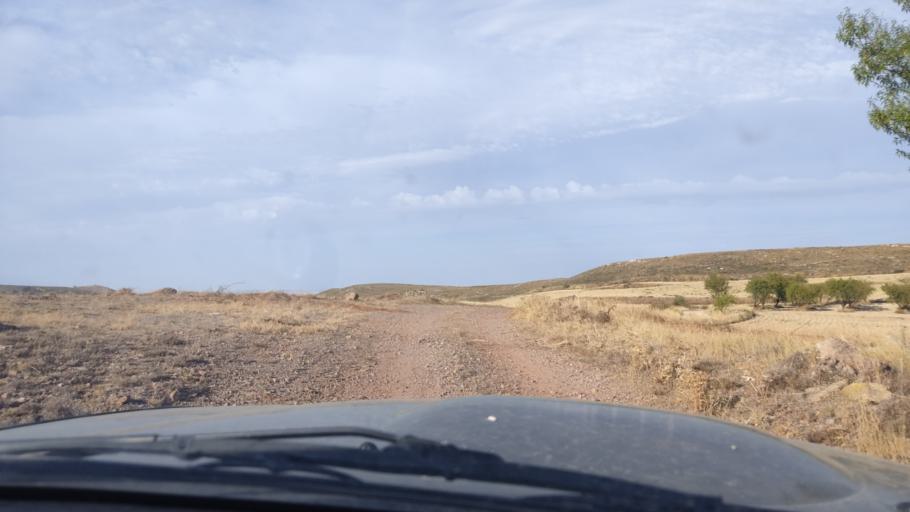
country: ES
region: Aragon
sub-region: Provincia de Teruel
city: Monforte de Moyuela
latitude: 41.0323
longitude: -1.0159
